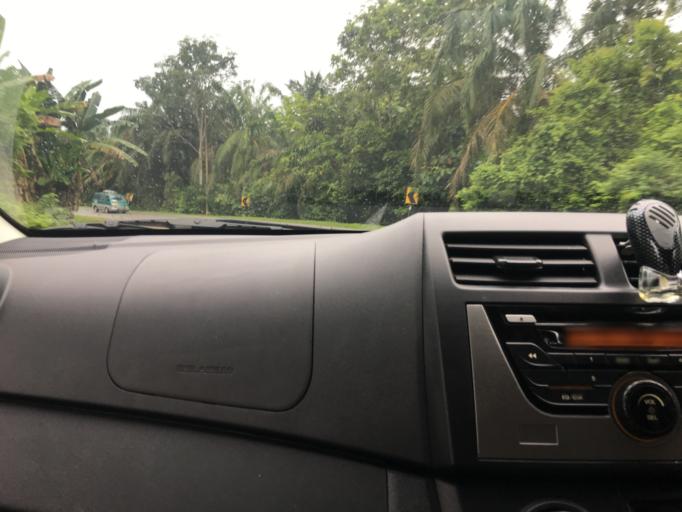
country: MY
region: Kedah
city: Bedong
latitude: 5.7117
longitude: 100.6314
